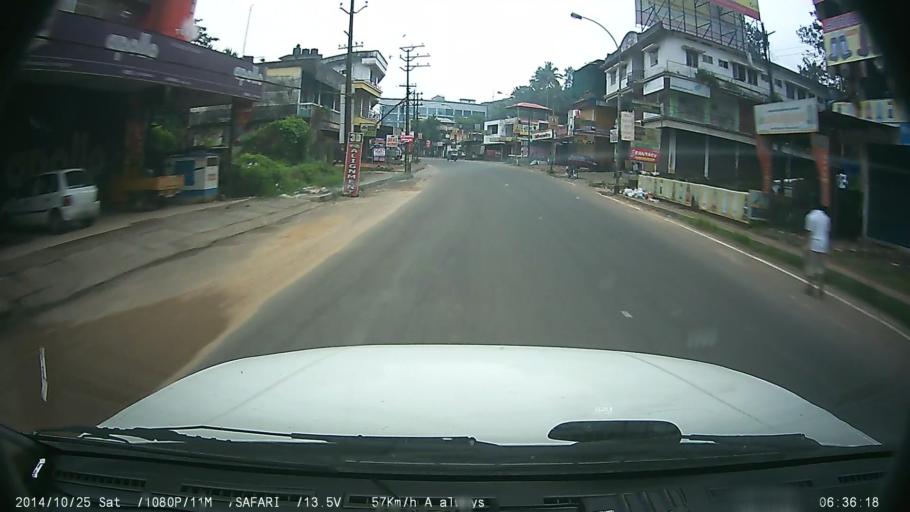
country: IN
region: Kerala
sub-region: Ernakulam
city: Muvattupula
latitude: 9.9949
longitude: 76.5727
